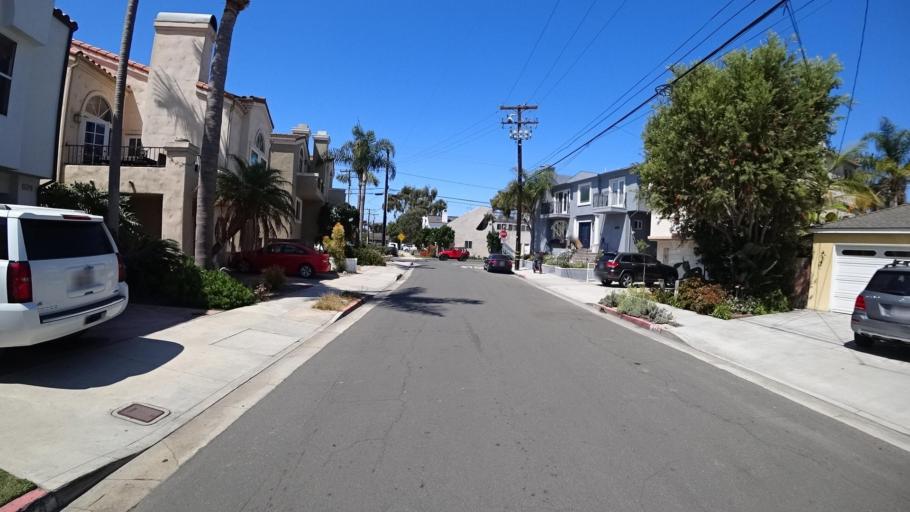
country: US
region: California
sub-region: Los Angeles County
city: Hermosa Beach
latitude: 33.8569
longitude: -118.3927
